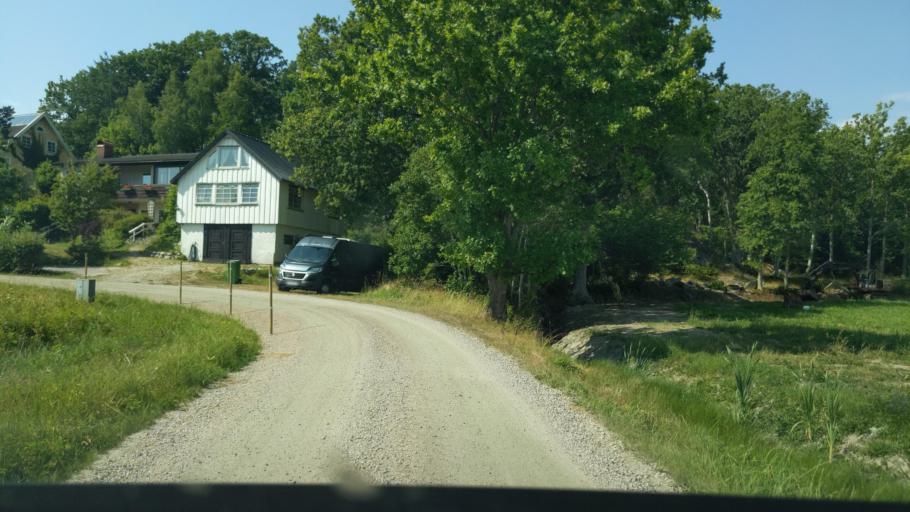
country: SE
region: Vaestra Goetaland
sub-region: Uddevalla Kommun
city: Uddevalla
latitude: 58.3362
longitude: 11.8001
